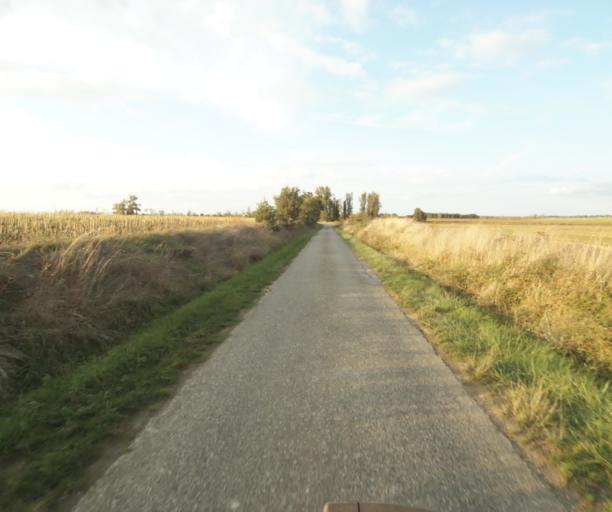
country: FR
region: Midi-Pyrenees
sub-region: Departement de la Haute-Garonne
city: Launac
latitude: 43.8106
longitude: 1.1638
